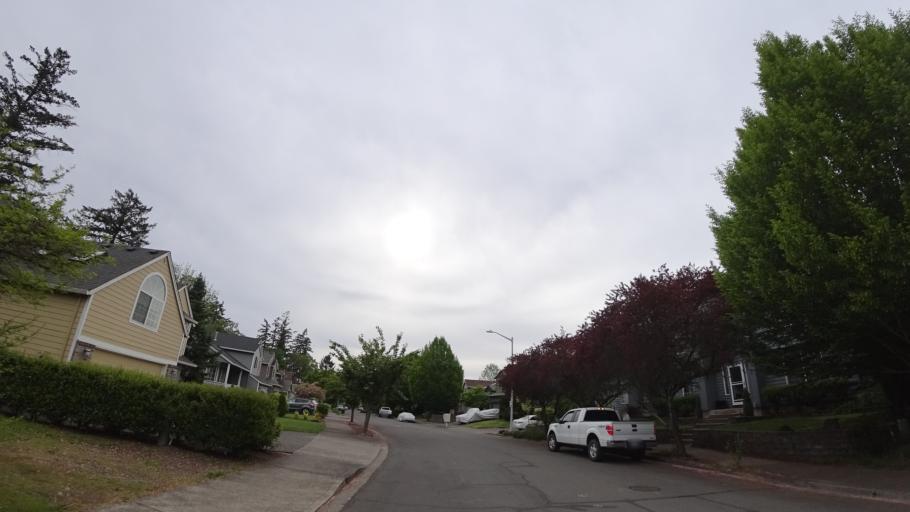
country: US
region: Oregon
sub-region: Washington County
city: Aloha
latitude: 45.5075
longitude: -122.9097
